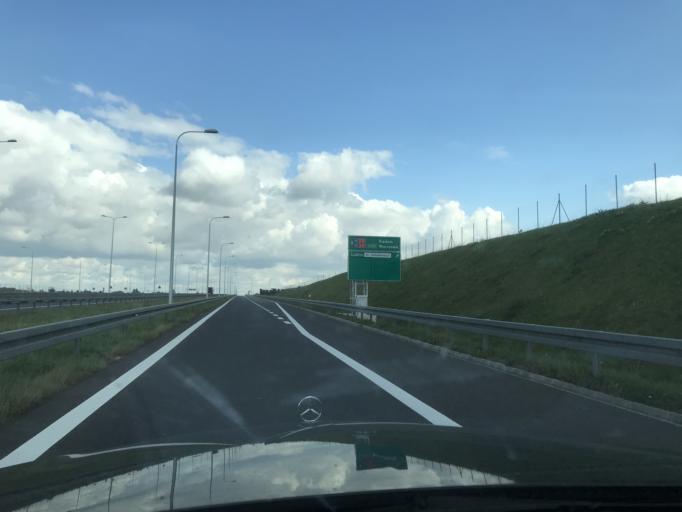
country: PL
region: Lublin Voivodeship
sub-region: Powiat lubelski
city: Jastkow
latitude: 51.2804
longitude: 22.4451
